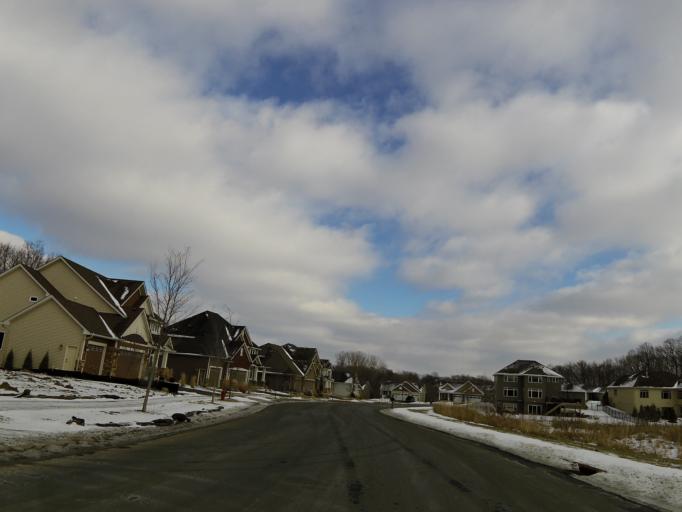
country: US
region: Minnesota
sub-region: Scott County
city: Prior Lake
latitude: 44.7329
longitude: -93.4448
